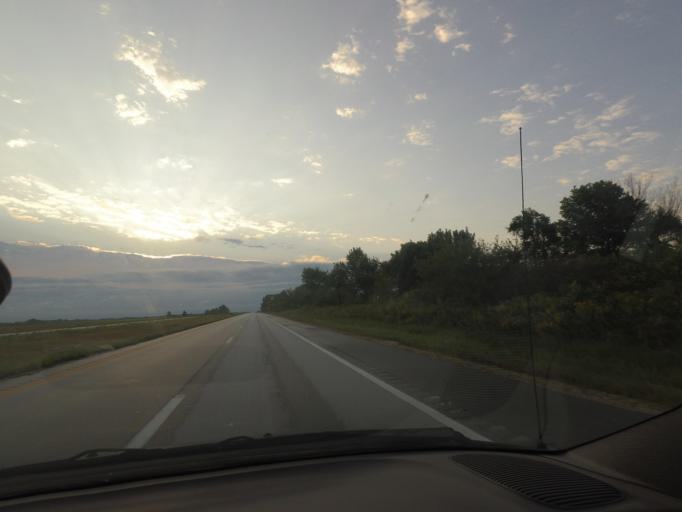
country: US
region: Missouri
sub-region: Shelby County
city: Shelbina
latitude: 39.7294
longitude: -92.1931
